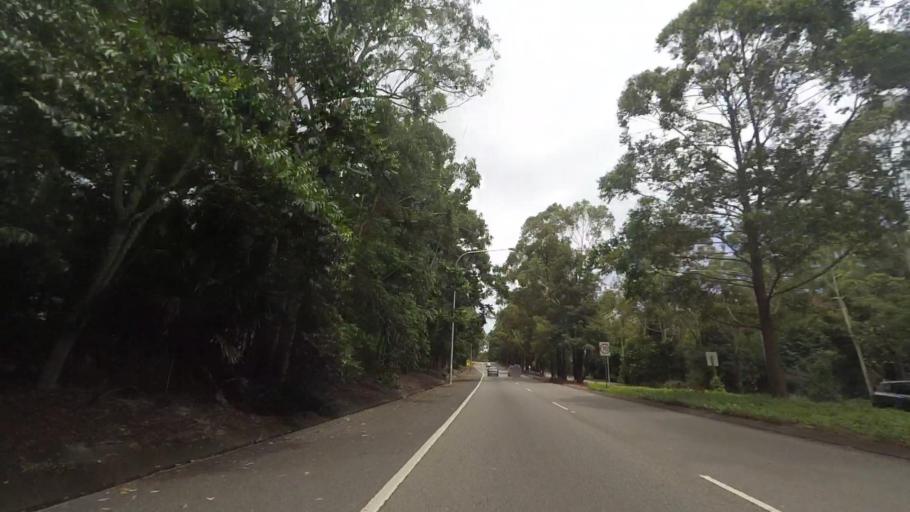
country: AU
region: New South Wales
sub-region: Wyong Shire
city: Berkeley Vale
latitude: -33.3466
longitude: 151.4305
